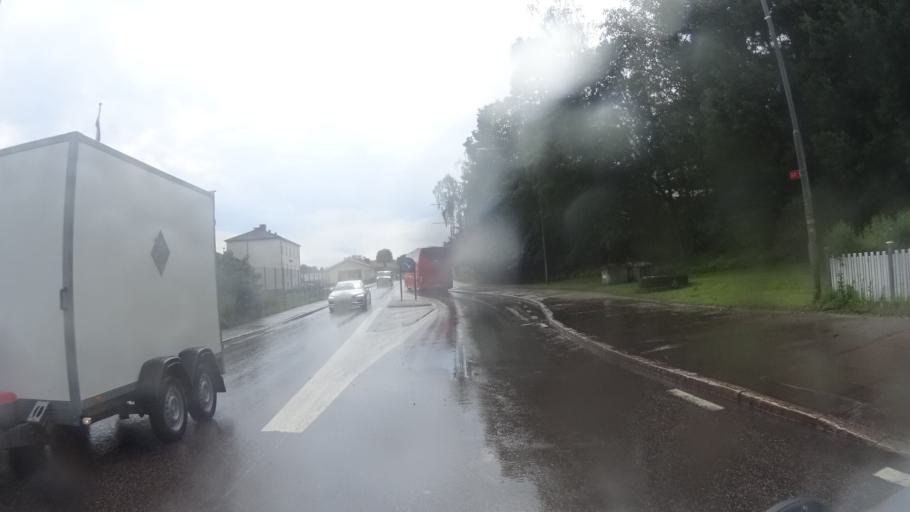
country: SE
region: OEstergoetland
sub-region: Kinda Kommun
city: Kisa
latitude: 57.9942
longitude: 15.6385
